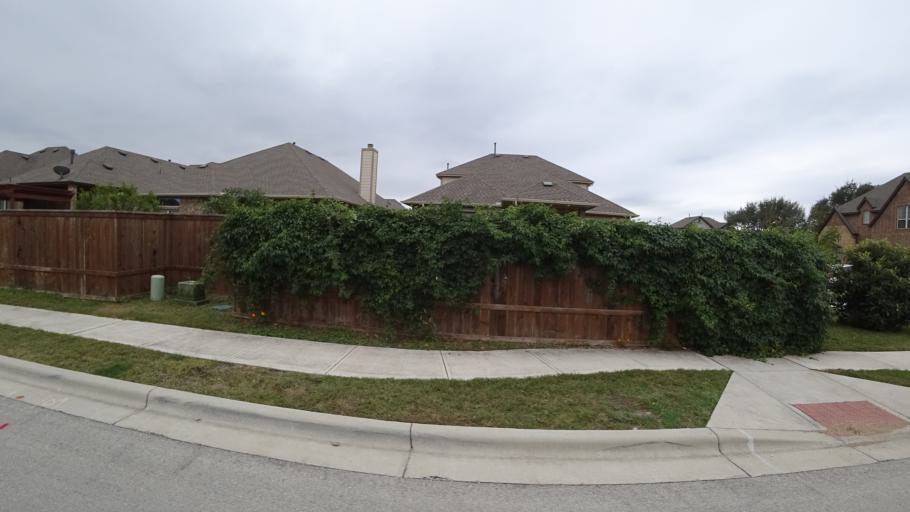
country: US
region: Texas
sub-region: Travis County
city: Manchaca
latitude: 30.1461
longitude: -97.8524
